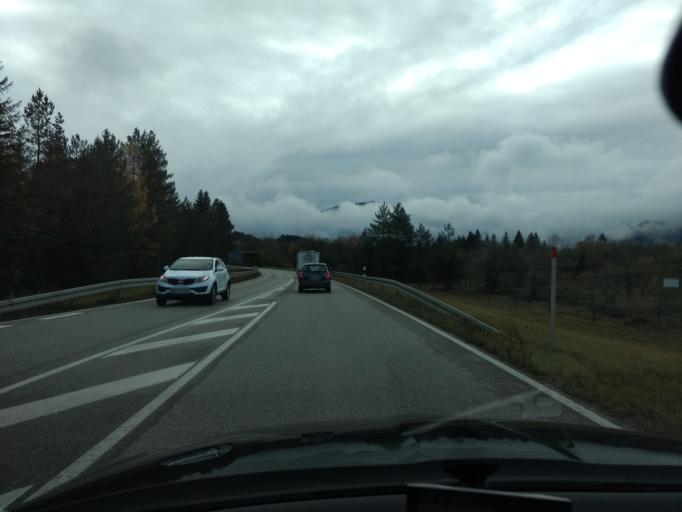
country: DE
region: Bavaria
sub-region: Upper Bavaria
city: Lenggries
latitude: 47.6606
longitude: 11.5848
